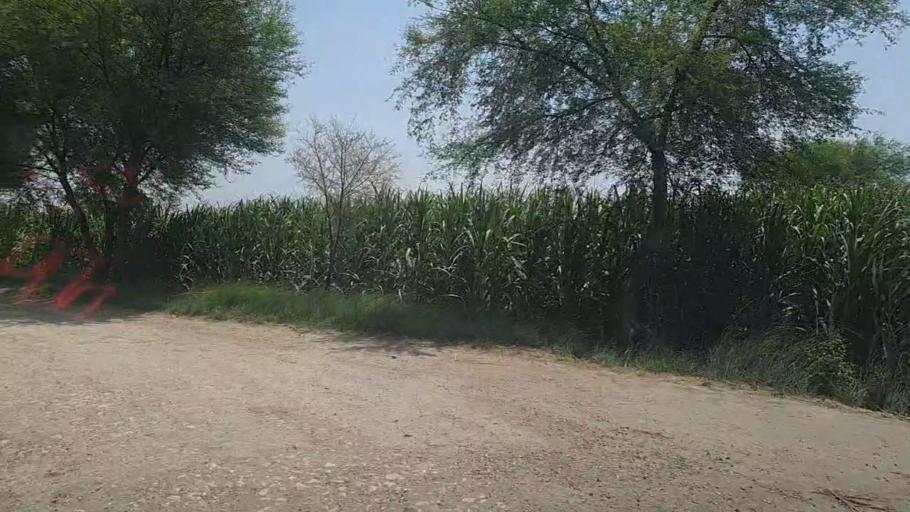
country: PK
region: Sindh
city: Ubauro
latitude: 28.2385
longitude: 69.8171
